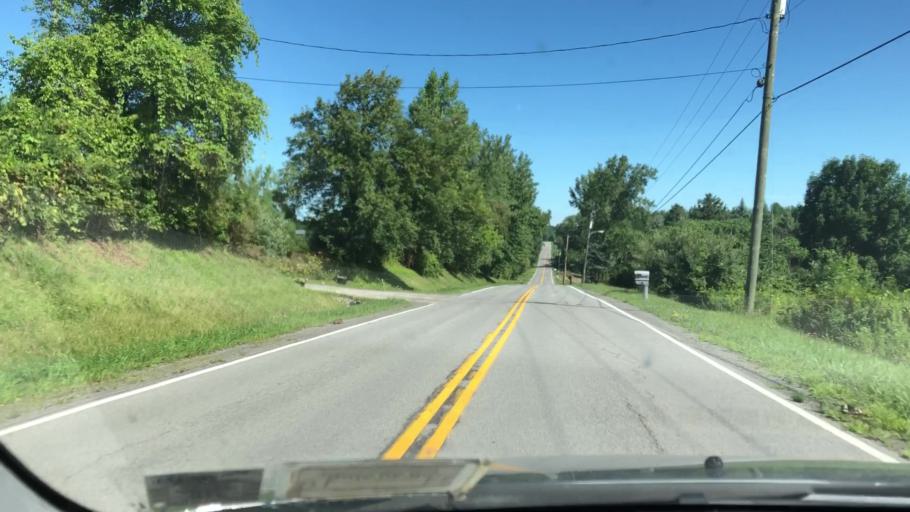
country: US
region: New York
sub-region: Monroe County
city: Fairport
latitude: 43.1107
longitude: -77.3730
